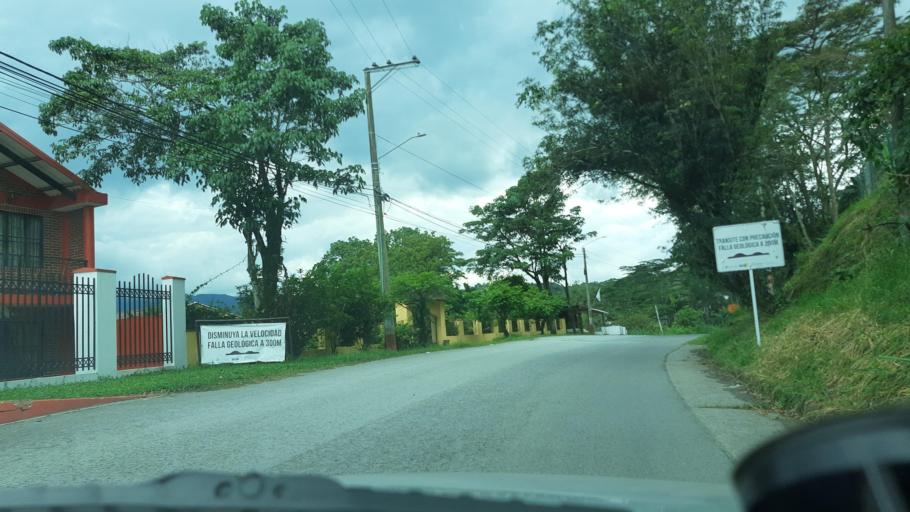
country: CO
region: Boyaca
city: Moniquira
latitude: 5.8843
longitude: -73.5771
